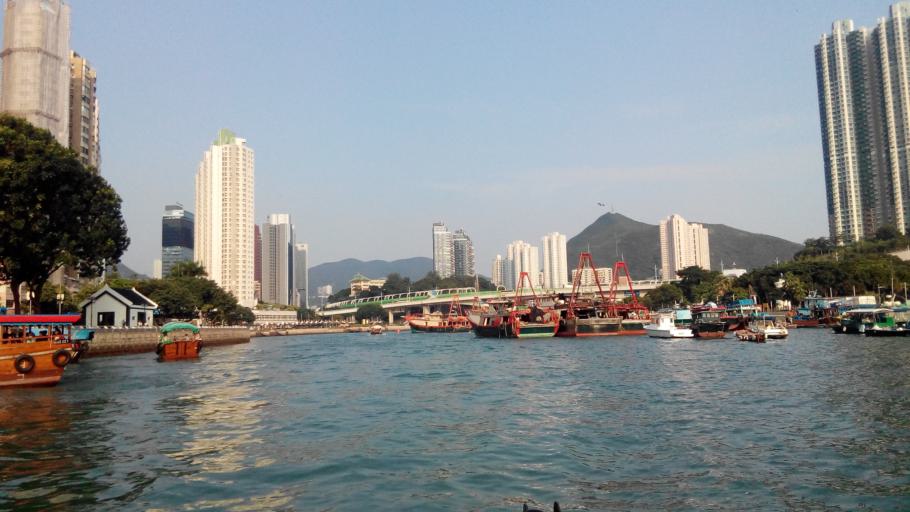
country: HK
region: Central and Western
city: Central
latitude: 22.2464
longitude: 114.1550
